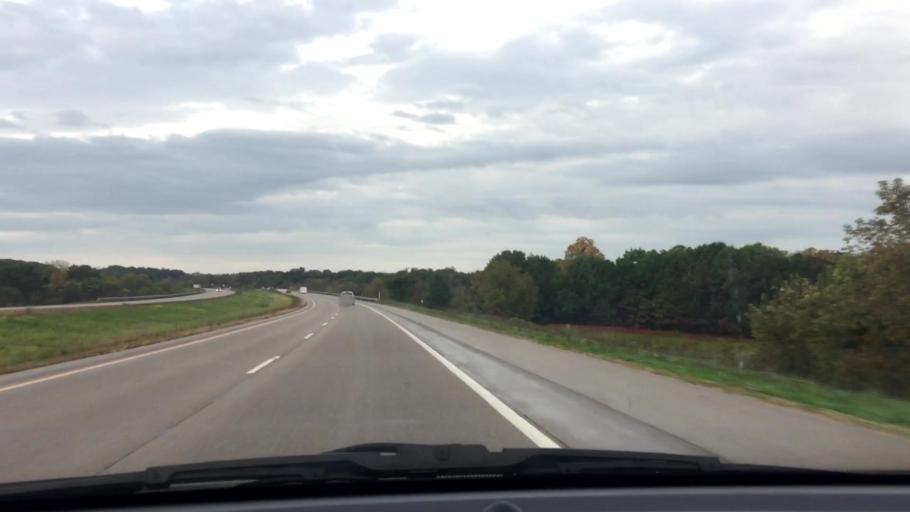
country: US
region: Wisconsin
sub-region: Rock County
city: Clinton
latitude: 42.5726
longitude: -88.8964
